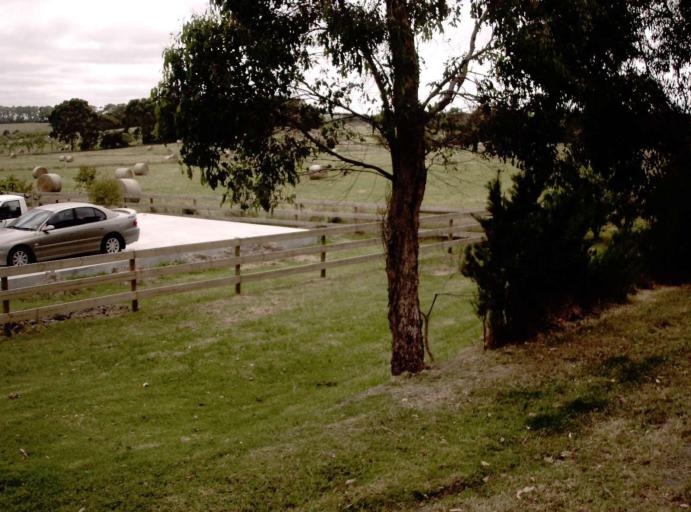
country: AU
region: Victoria
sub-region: Cardinia
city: Koo-Wee-Rup
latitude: -38.3332
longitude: 145.6778
